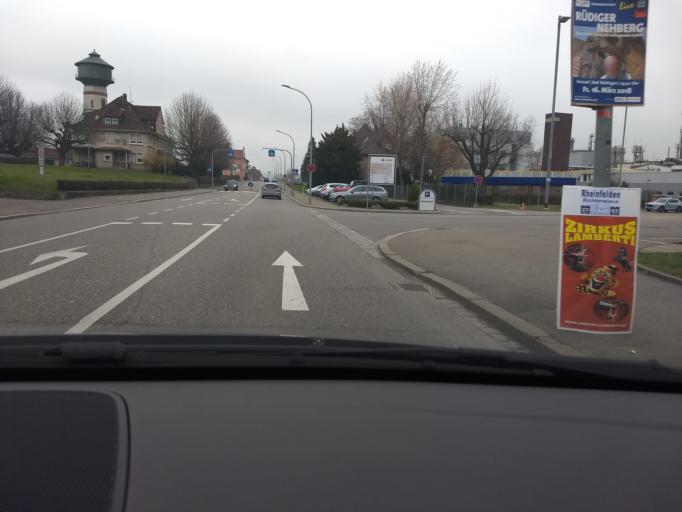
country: DE
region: Baden-Wuerttemberg
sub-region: Freiburg Region
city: Rheinfelden (Baden)
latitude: 47.5630
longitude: 7.7932
